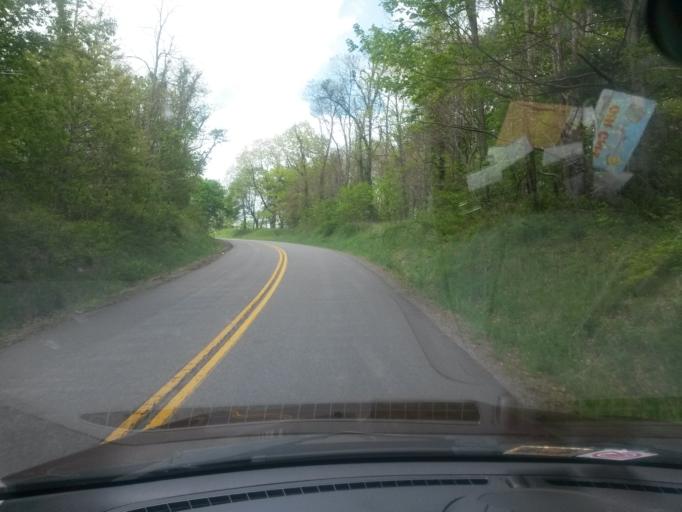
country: US
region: Virginia
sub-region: Floyd County
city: Floyd
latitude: 36.7907
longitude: -80.3872
